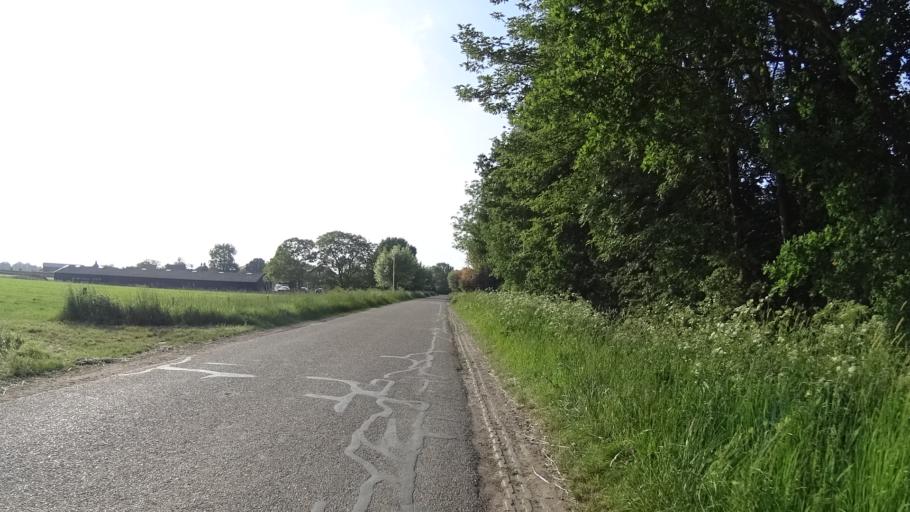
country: NL
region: North Brabant
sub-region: Gemeente Heusden
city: Heusden
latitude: 51.7239
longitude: 5.1575
